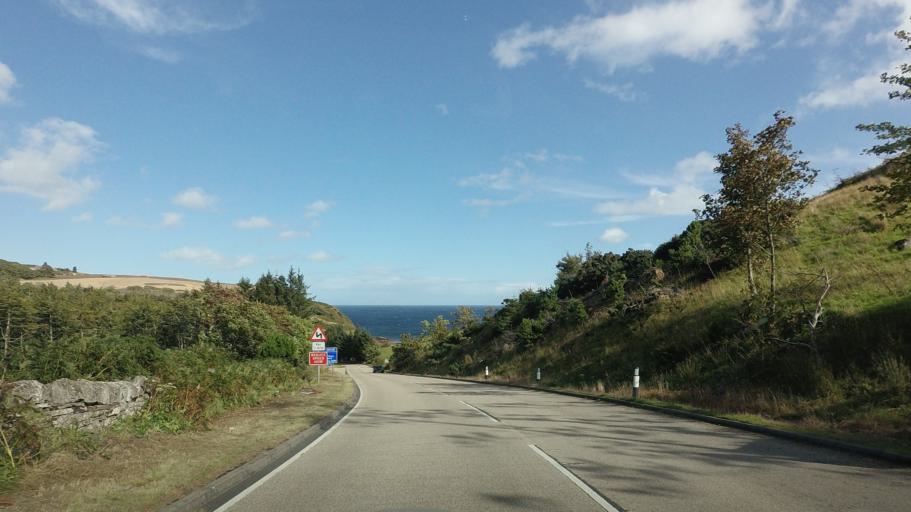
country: GB
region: Scotland
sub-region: Highland
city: Brora
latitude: 58.1817
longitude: -3.5035
